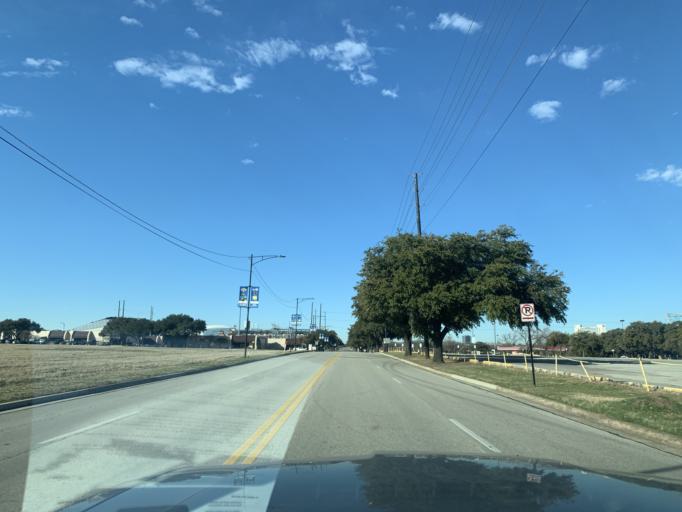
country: US
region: Texas
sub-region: Tarrant County
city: Arlington
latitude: 32.7525
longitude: -97.0699
